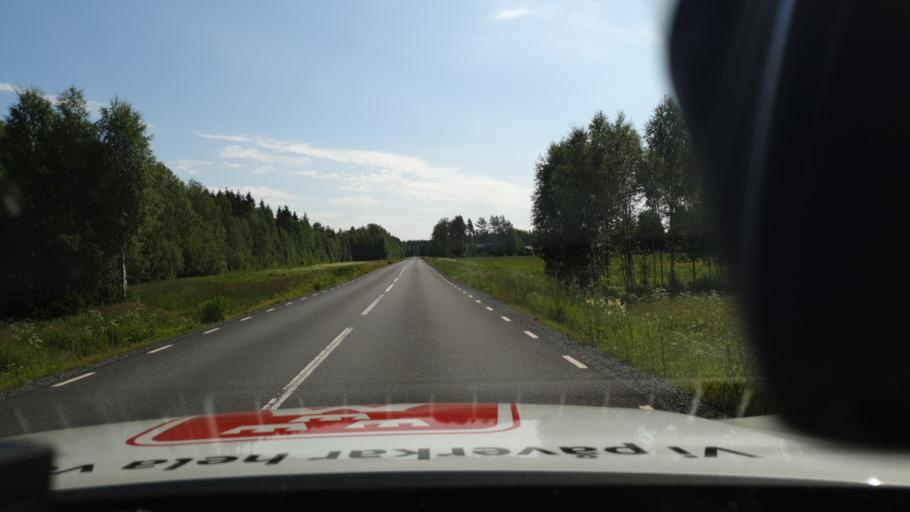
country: SE
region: Norrbotten
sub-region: Bodens Kommun
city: Boden
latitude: 65.8436
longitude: 21.7456
